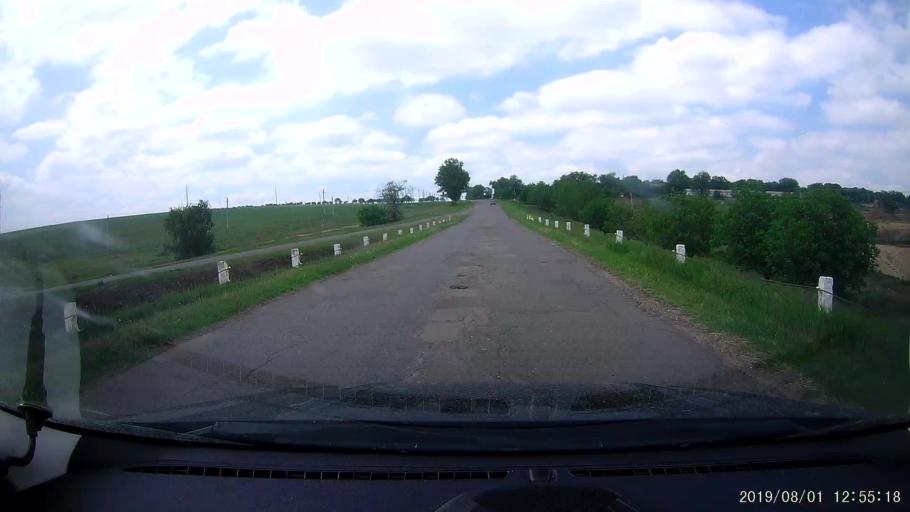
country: MD
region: Gagauzia
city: Vulcanesti
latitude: 45.6940
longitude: 28.4697
